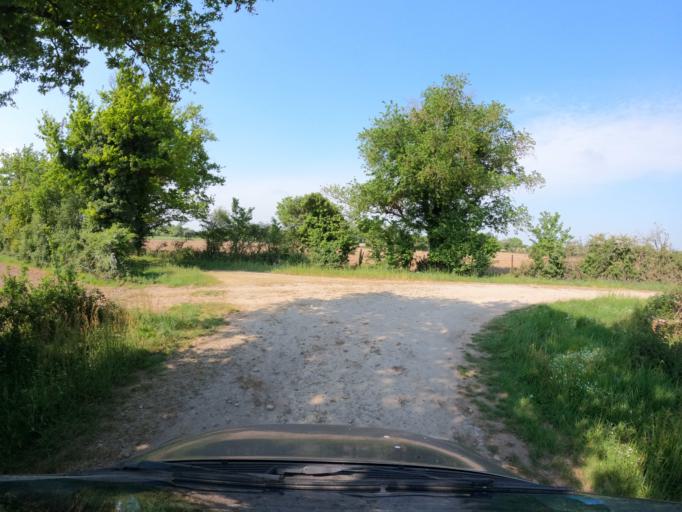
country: FR
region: Pays de la Loire
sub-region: Departement de la Vendee
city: Treize-Septiers
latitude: 47.0016
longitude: -1.2493
